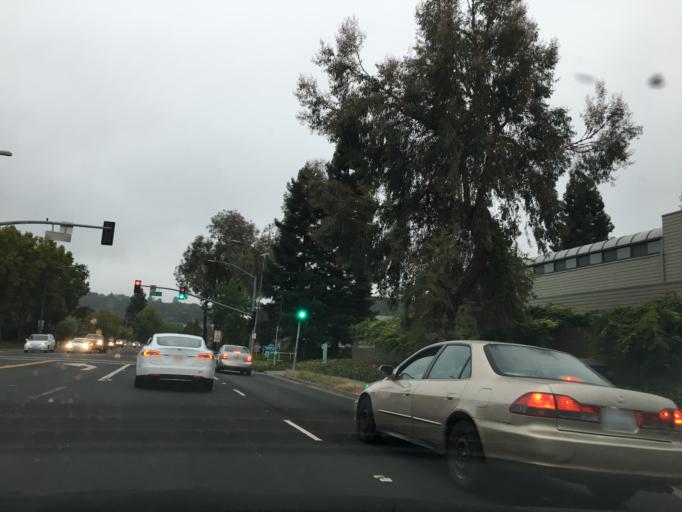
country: US
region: California
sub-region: Sonoma County
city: Santa Rosa
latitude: 38.4423
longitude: -122.6874
